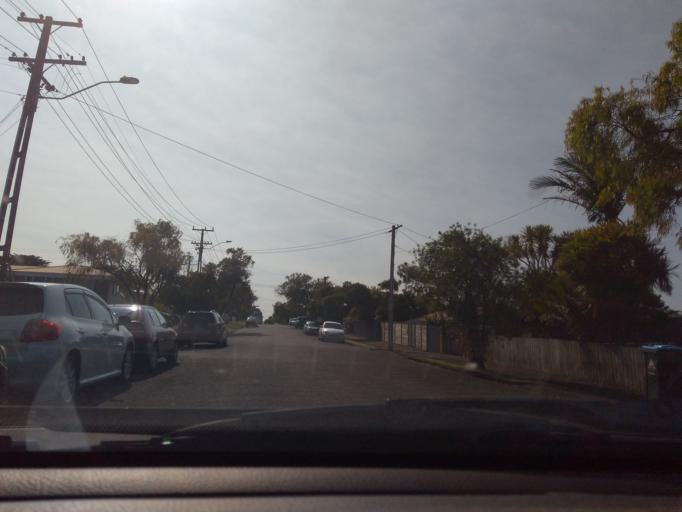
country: NZ
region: Auckland
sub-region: Auckland
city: Waitakere
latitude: -36.9222
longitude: 174.6959
